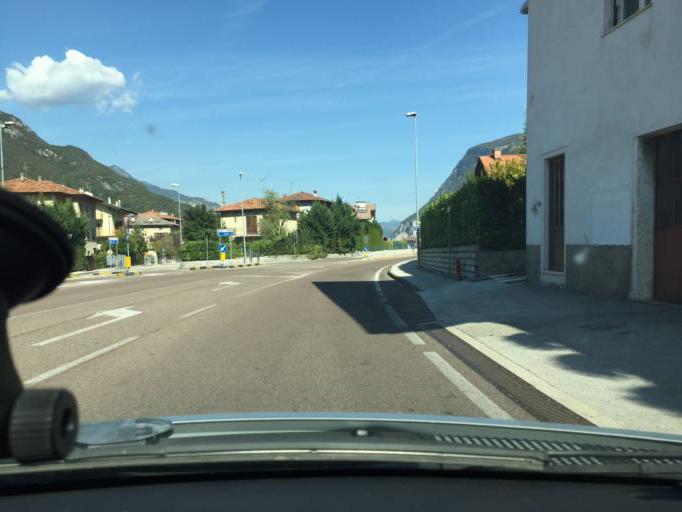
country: IT
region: Trentino-Alto Adige
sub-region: Provincia di Trento
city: Calliano
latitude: 45.9296
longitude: 11.0931
